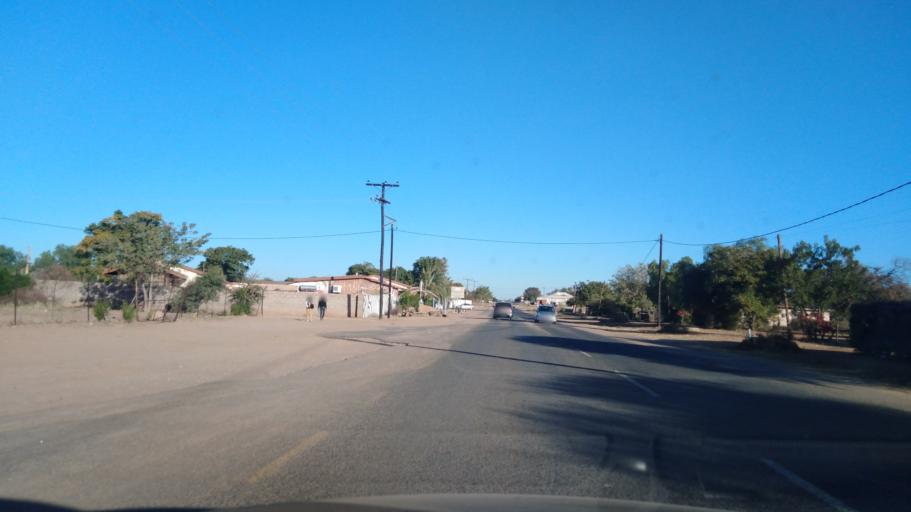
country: BW
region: Central
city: Mahalapye
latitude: -23.0824
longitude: 26.8230
